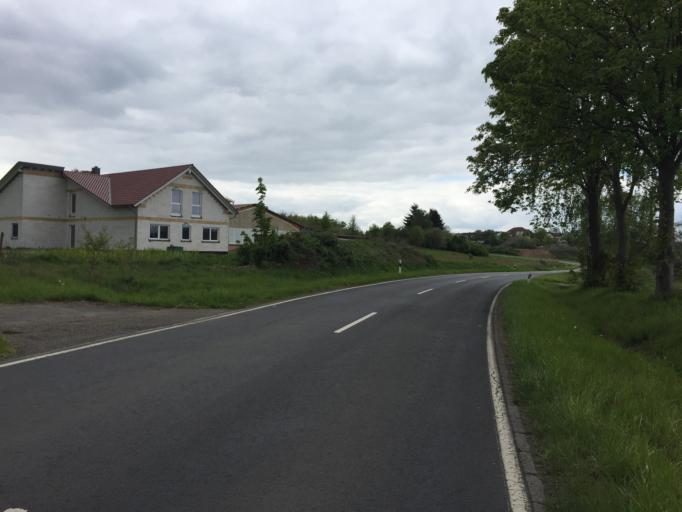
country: DE
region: Hesse
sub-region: Regierungsbezirk Giessen
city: Reiskirchen
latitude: 50.5737
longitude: 8.8295
